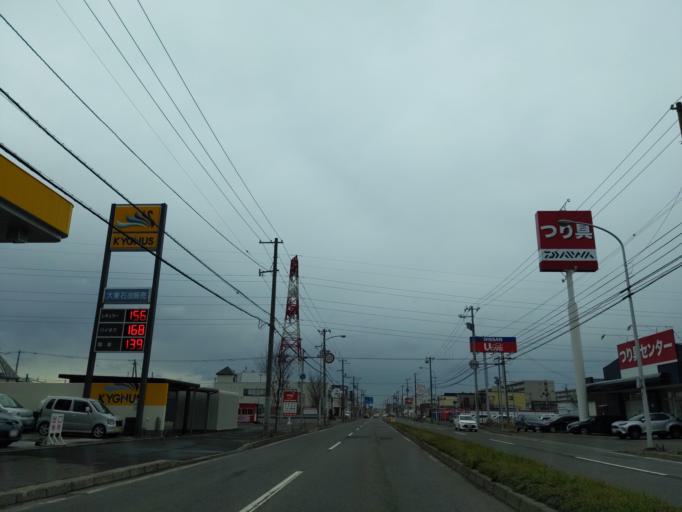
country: JP
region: Hokkaido
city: Sapporo
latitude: 43.1008
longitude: 141.4073
